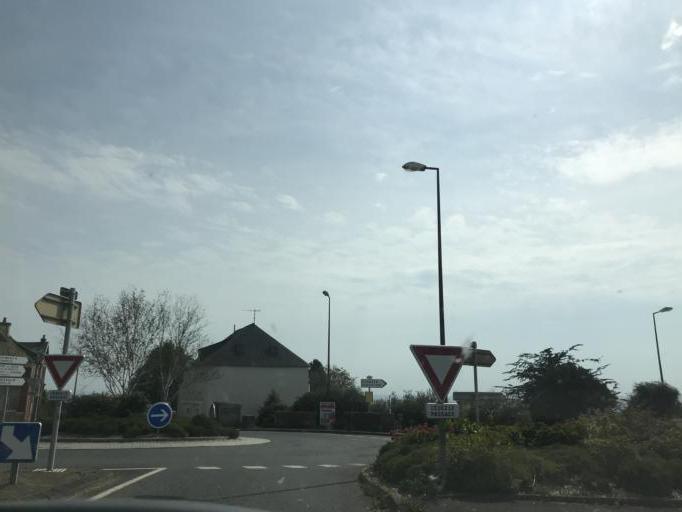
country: FR
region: Brittany
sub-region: Departement du Finistere
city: Hanvec
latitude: 48.2851
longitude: -4.1214
